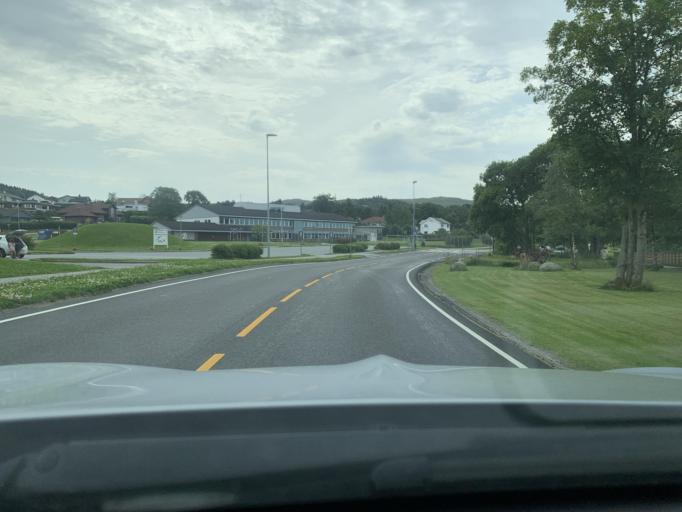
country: NO
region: Rogaland
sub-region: Sandnes
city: Sandnes
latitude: 58.7734
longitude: 5.7255
